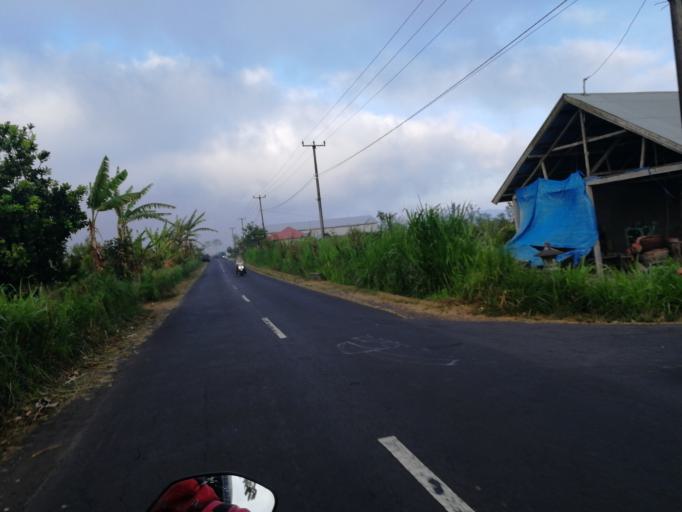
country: ID
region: Bali
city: Banjar Kedisan
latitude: -8.2225
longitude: 115.2636
